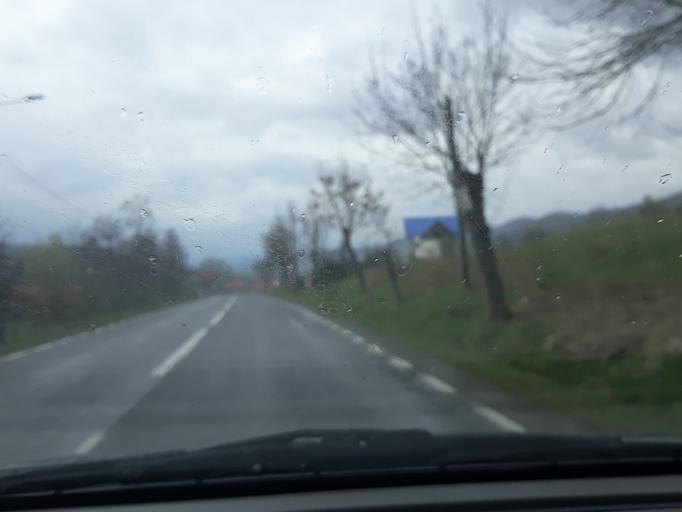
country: RO
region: Harghita
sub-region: Comuna Corund
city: Corund
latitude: 46.4842
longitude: 25.1707
